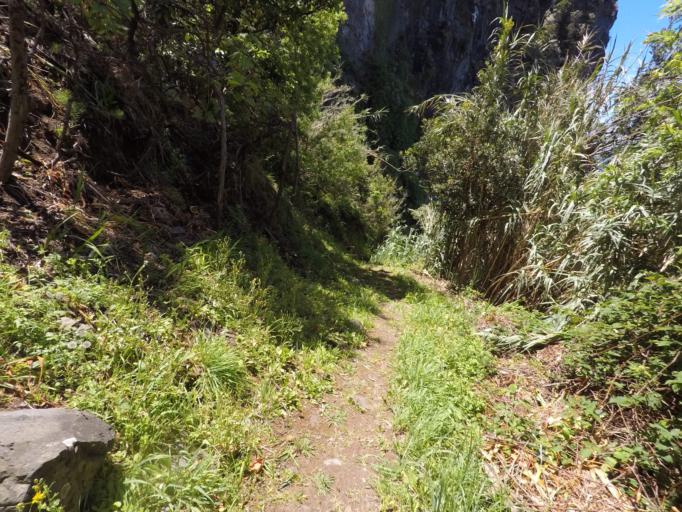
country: PT
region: Madeira
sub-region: Sao Vicente
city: Sao Vicente
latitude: 32.8256
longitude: -16.9824
